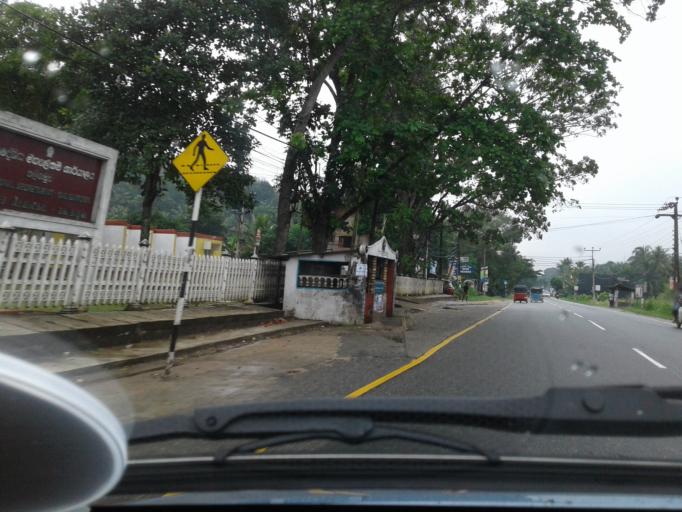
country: LK
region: Central
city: Kadugannawa
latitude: 7.2365
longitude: 80.2915
